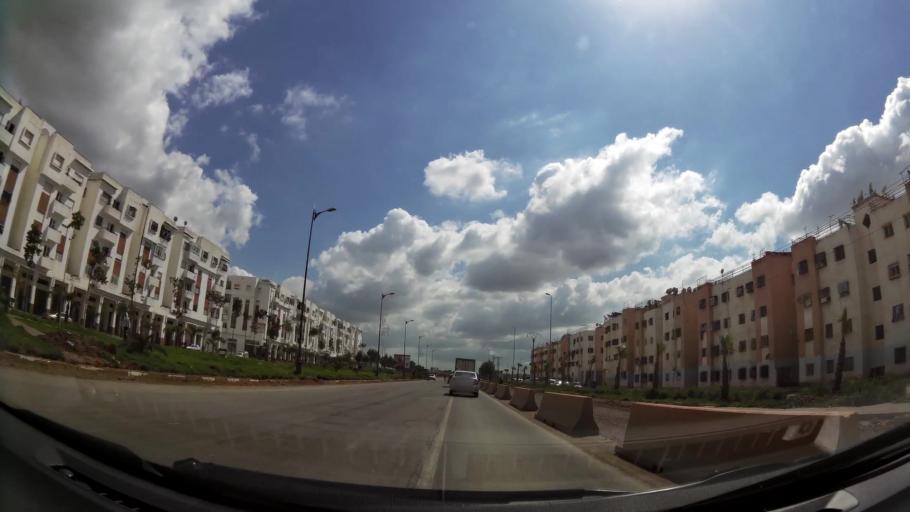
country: MA
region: Chaouia-Ouardigha
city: Nouaseur
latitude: 33.3638
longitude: -7.5453
